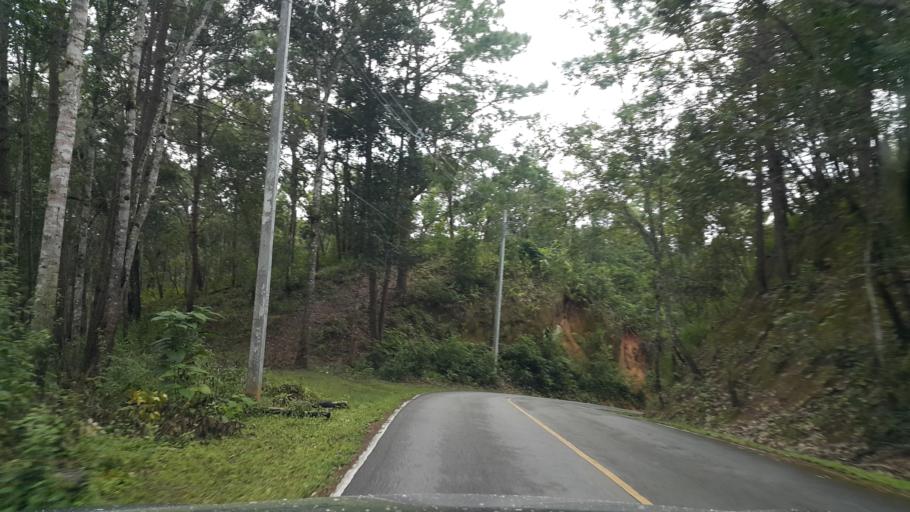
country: TH
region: Chiang Mai
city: Chaem Luang
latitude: 18.9138
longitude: 98.4953
